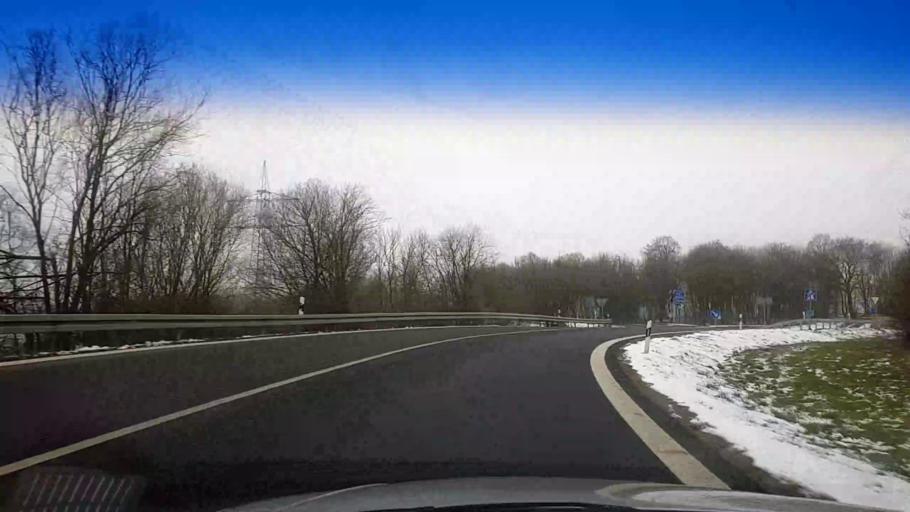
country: DE
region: Bavaria
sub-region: Upper Franconia
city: Ebensfeld
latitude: 50.0590
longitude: 10.9683
